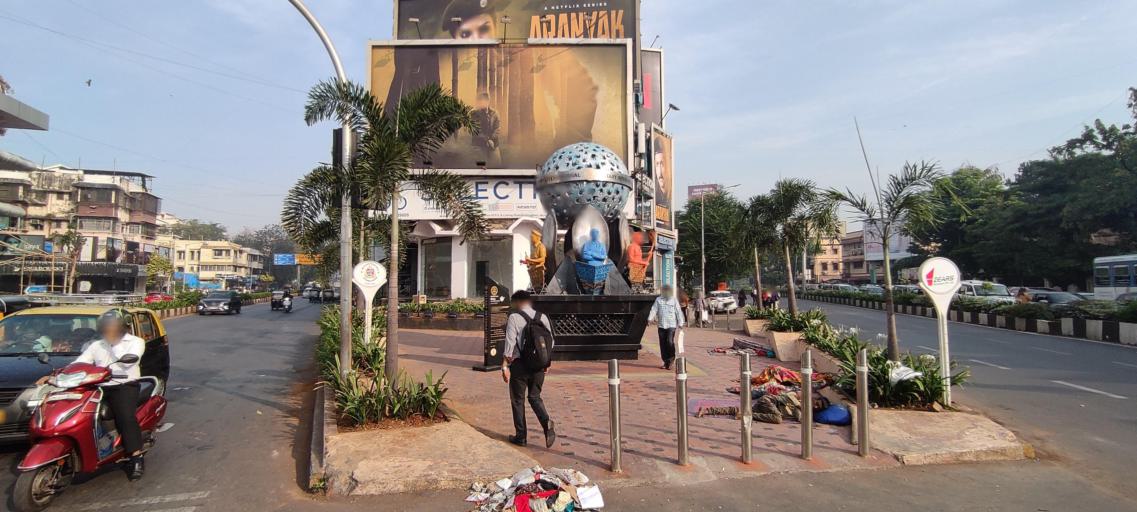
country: IN
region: Maharashtra
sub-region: Mumbai Suburban
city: Mumbai
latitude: 19.0597
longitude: 72.8369
